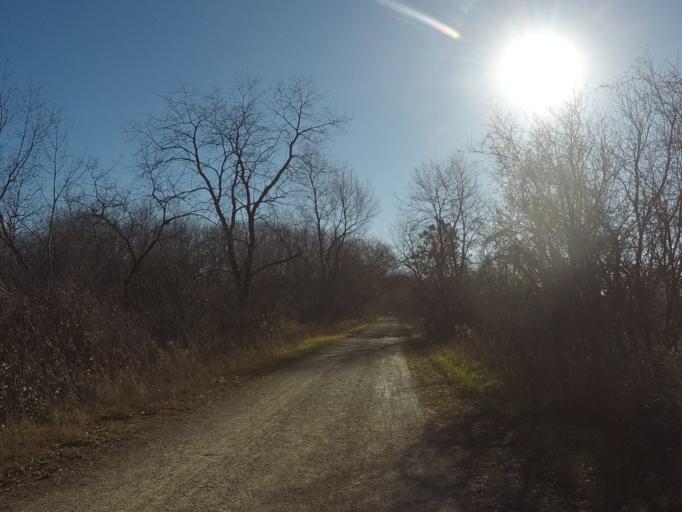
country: US
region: Wisconsin
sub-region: Dane County
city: Deerfield
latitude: 43.0508
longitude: -89.0637
